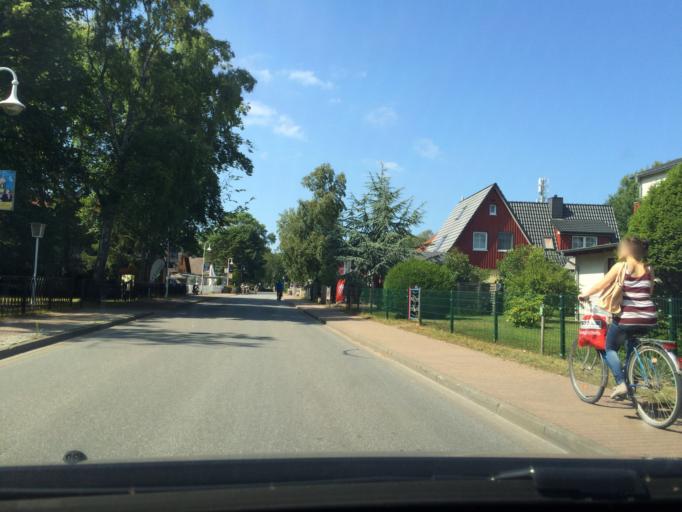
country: DE
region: Mecklenburg-Vorpommern
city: Ostseebad Prerow
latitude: 54.4446
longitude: 12.5768
